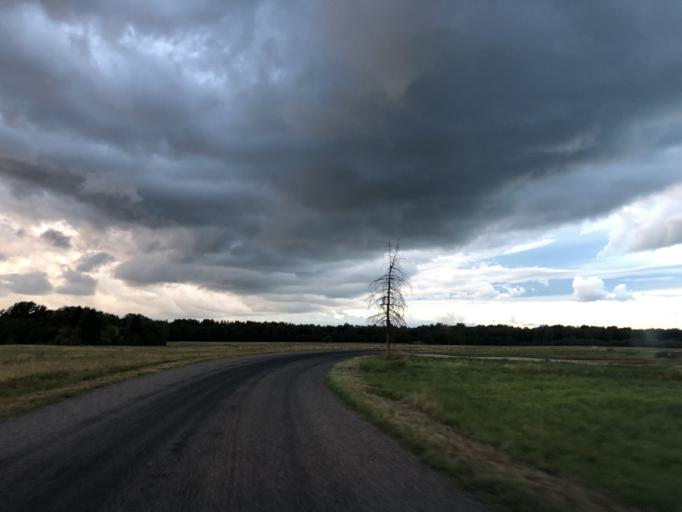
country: EE
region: Laeaene
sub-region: Ridala Parish
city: Uuemoisa
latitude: 58.8870
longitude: 23.6610
